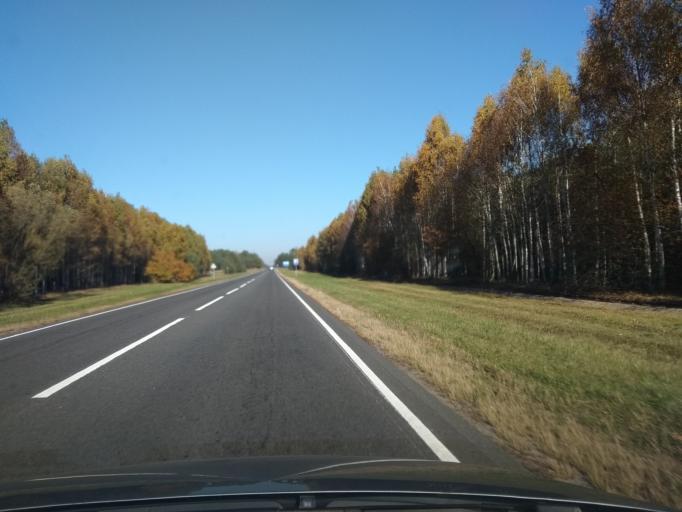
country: BY
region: Brest
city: Kobryn
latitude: 52.0683
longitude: 24.2839
